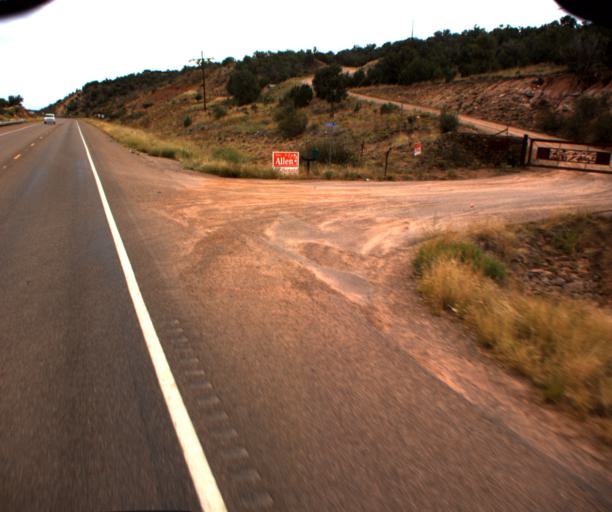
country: US
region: Arizona
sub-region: Navajo County
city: Taylor
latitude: 34.4035
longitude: -110.0745
